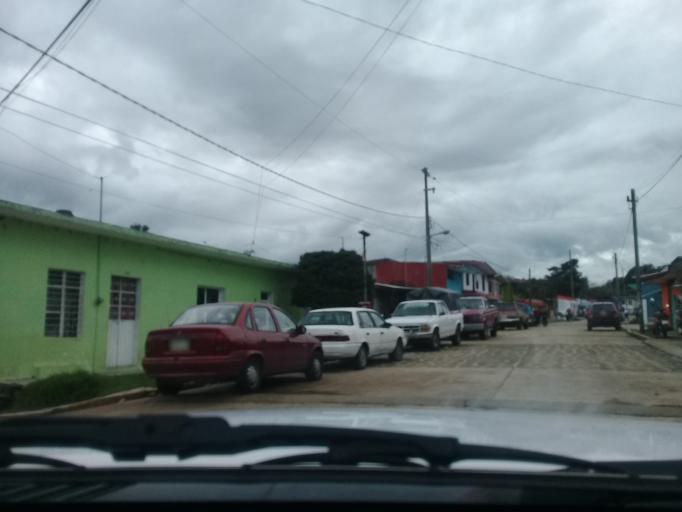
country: MX
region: Veracruz
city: Rafael Lucio
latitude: 19.5920
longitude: -96.9904
